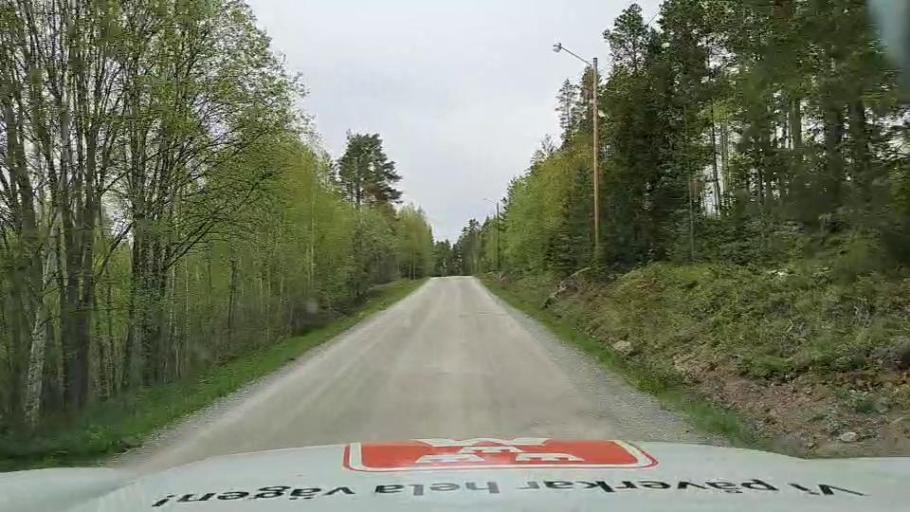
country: SE
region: Jaemtland
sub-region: Bergs Kommun
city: Hoverberg
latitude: 62.8849
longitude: 14.6582
